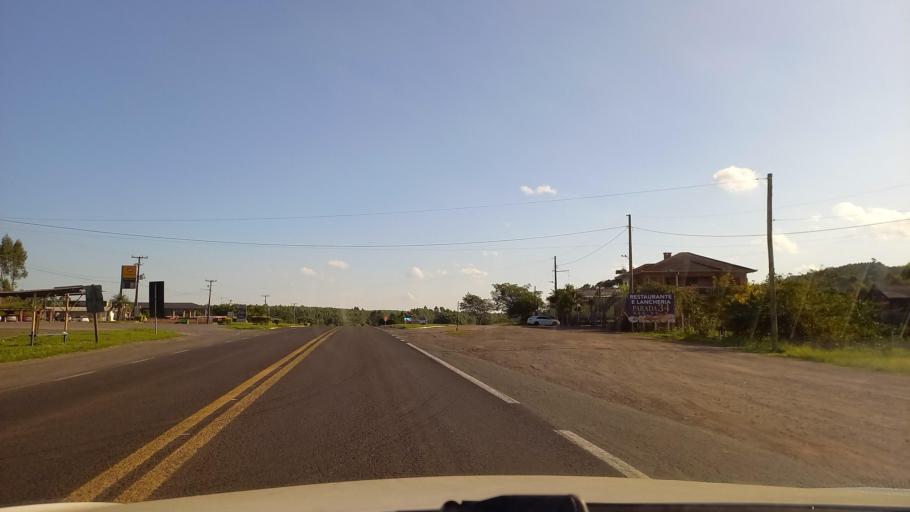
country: BR
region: Rio Grande do Sul
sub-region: Taquari
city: Taquari
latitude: -29.7089
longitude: -51.7648
